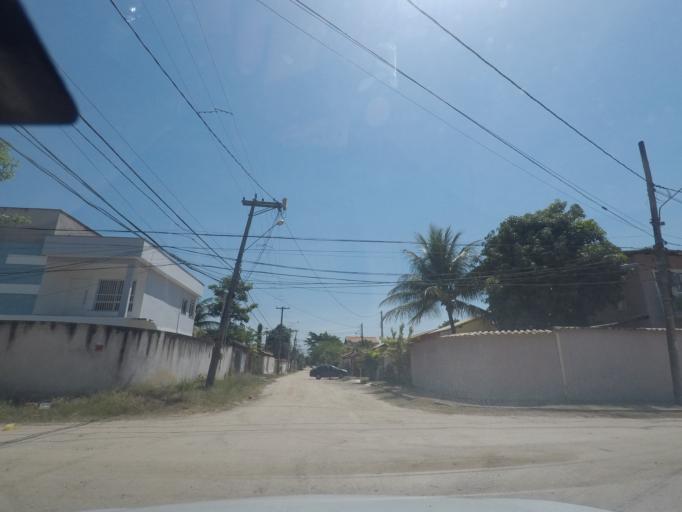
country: BR
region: Rio de Janeiro
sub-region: Niteroi
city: Niteroi
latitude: -22.9348
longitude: -43.0156
